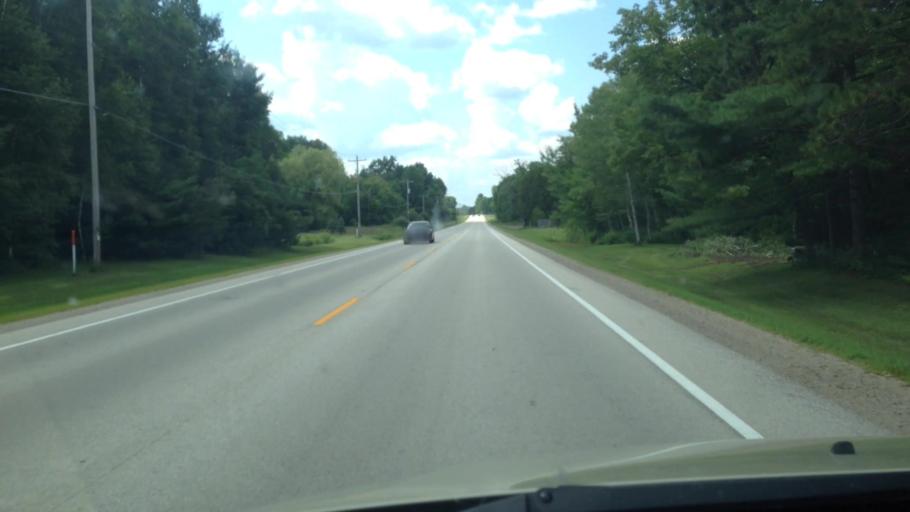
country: US
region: Wisconsin
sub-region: Brown County
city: Suamico
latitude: 44.6400
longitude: -88.0752
